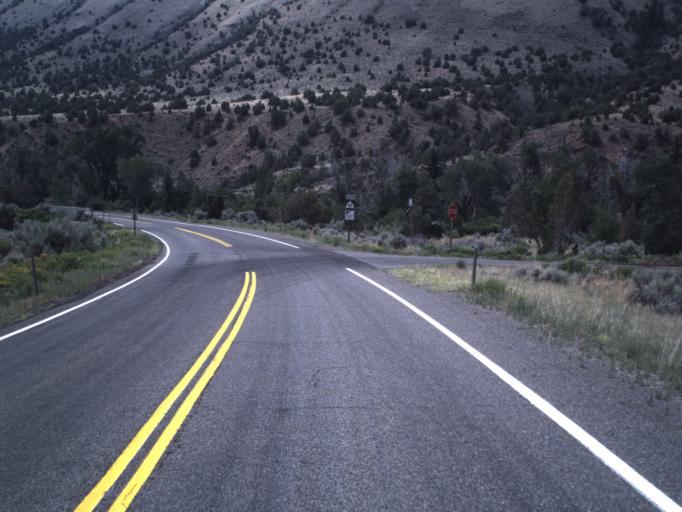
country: US
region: Utah
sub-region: Daggett County
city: Manila
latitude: 40.9296
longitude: -109.7215
